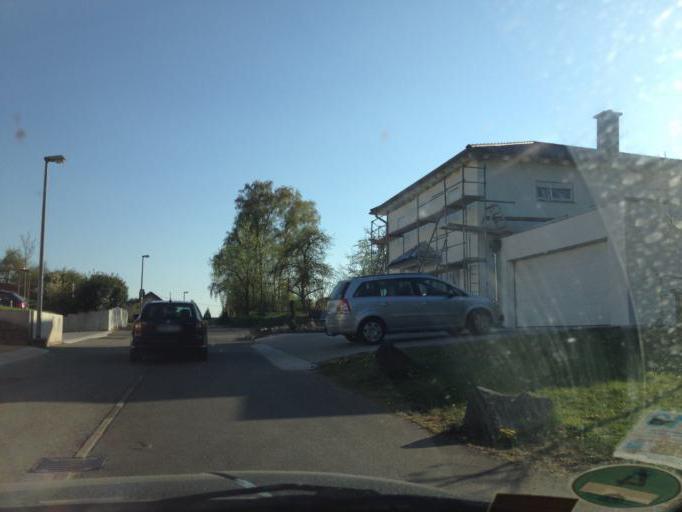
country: DE
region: Saarland
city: Sankt Wendel
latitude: 49.4776
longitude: 7.1807
